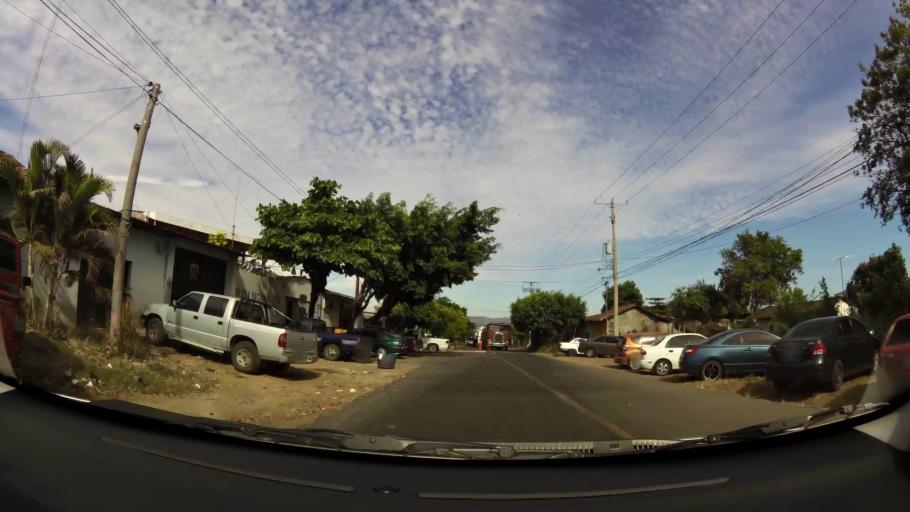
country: SV
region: Santa Ana
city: Chalchuapa
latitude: 13.9810
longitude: -89.6846
